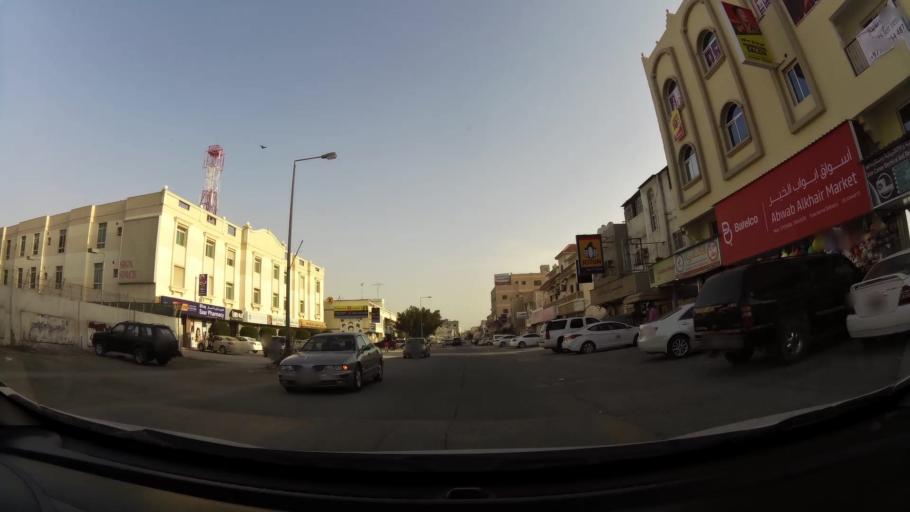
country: BH
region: Manama
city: Jidd Hafs
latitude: 26.1963
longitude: 50.4861
